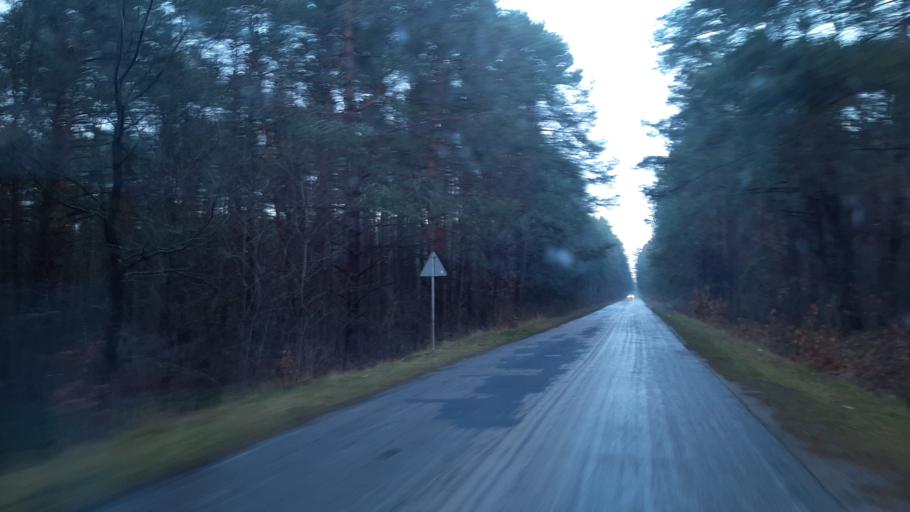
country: PL
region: Lublin Voivodeship
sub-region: Powiat lubartowski
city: Kamionka
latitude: 51.4808
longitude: 22.4714
